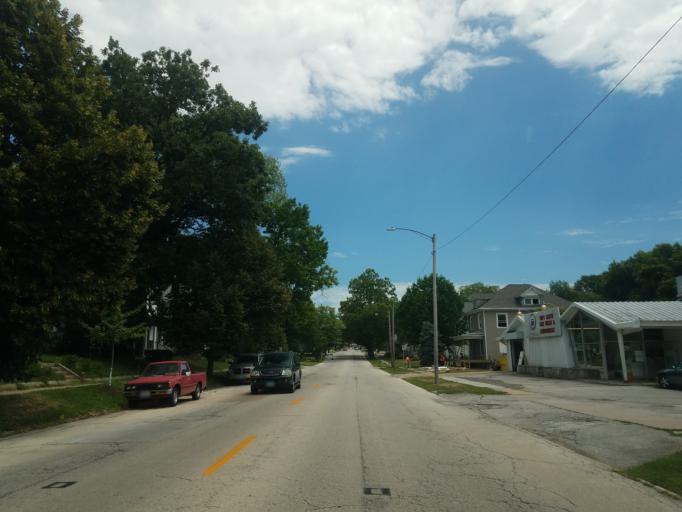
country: US
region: Illinois
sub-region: McLean County
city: Bloomington
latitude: 40.4822
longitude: -89.0011
